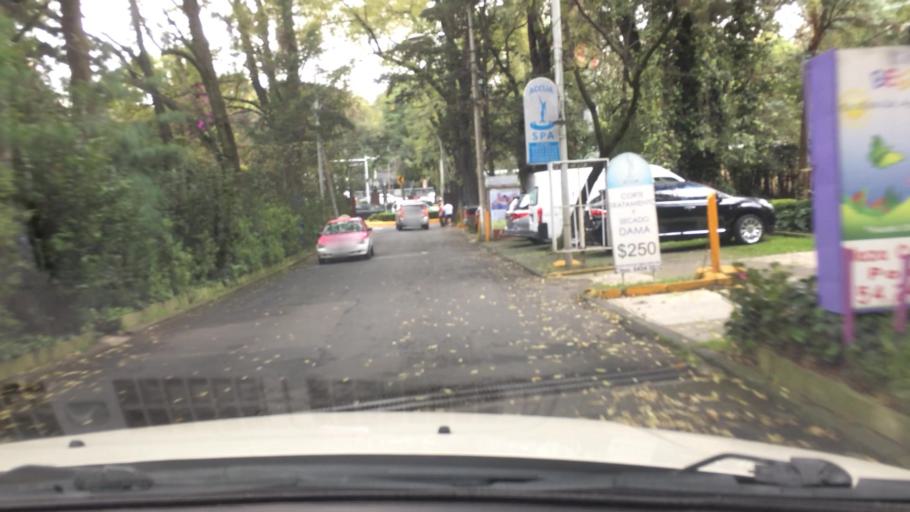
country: MX
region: Mexico City
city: Tlalpan
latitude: 19.2962
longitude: -99.1825
